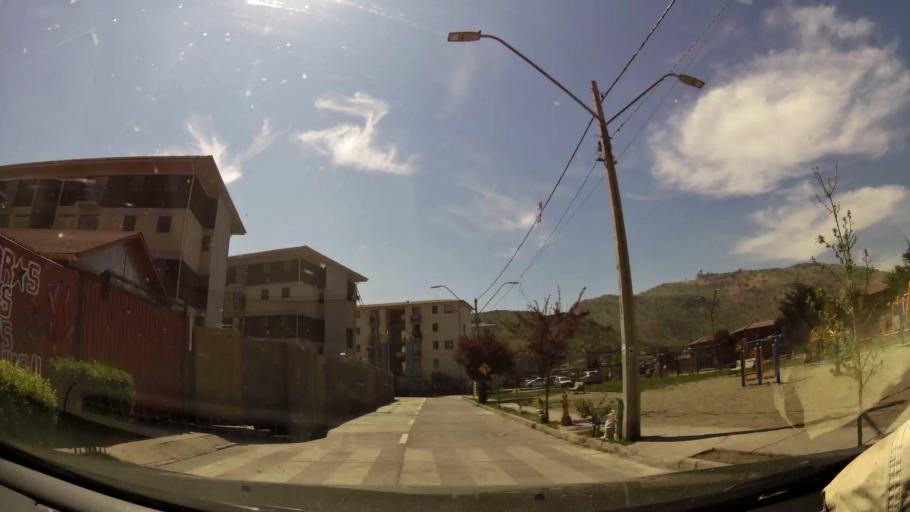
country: CL
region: Santiago Metropolitan
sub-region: Provincia de Santiago
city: Lo Prado
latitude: -33.3949
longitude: -70.7518
